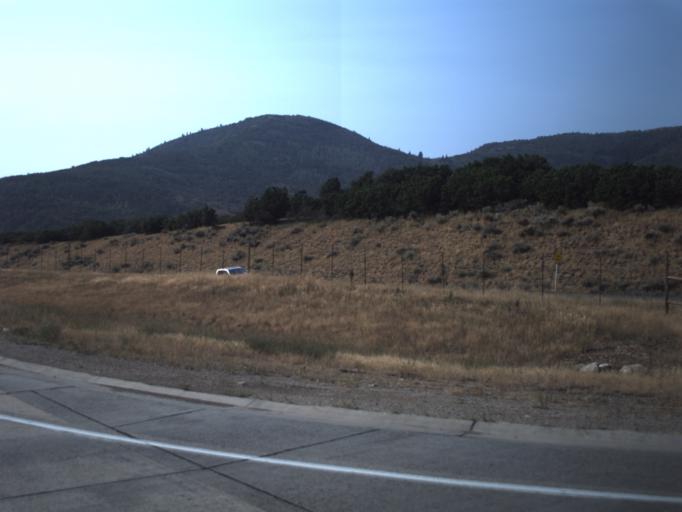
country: US
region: Utah
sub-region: Summit County
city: Park City
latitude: 40.6247
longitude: -111.4415
